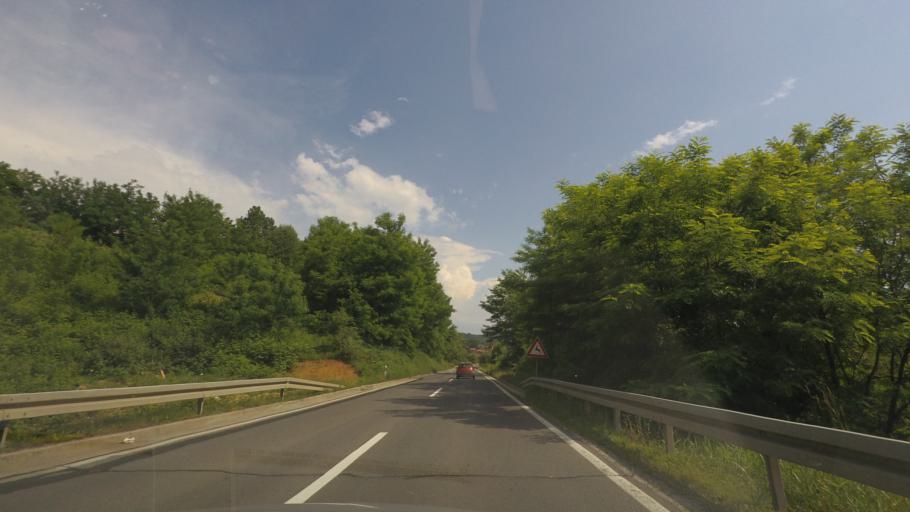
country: HR
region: Karlovacka
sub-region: Grad Karlovac
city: Karlovac
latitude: 45.4400
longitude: 15.4956
